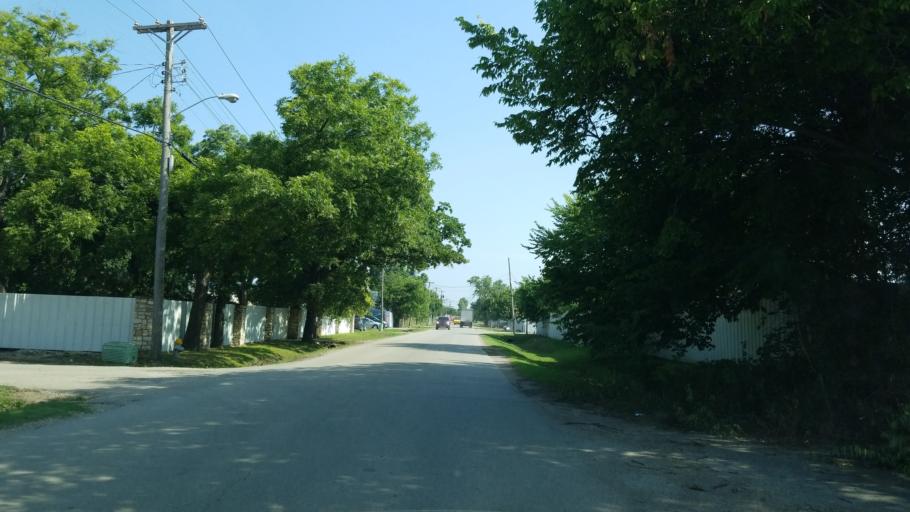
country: US
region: Texas
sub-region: Dallas County
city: Farmers Branch
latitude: 32.8716
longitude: -96.9024
